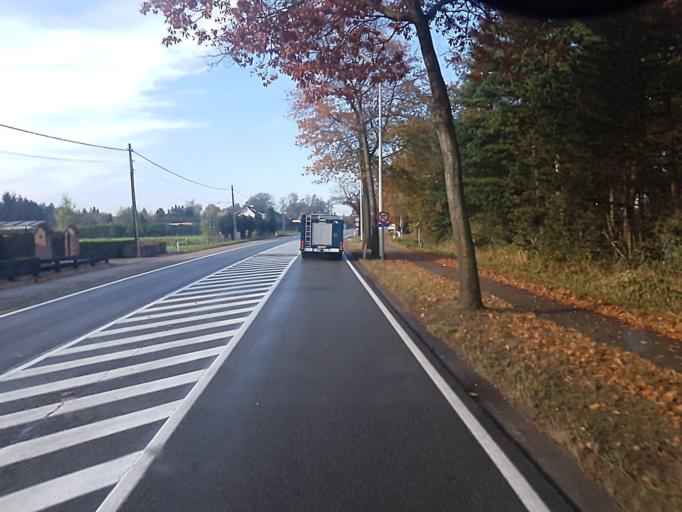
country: BE
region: Flanders
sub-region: Provincie Antwerpen
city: Beerse
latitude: 51.3022
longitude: 4.7974
